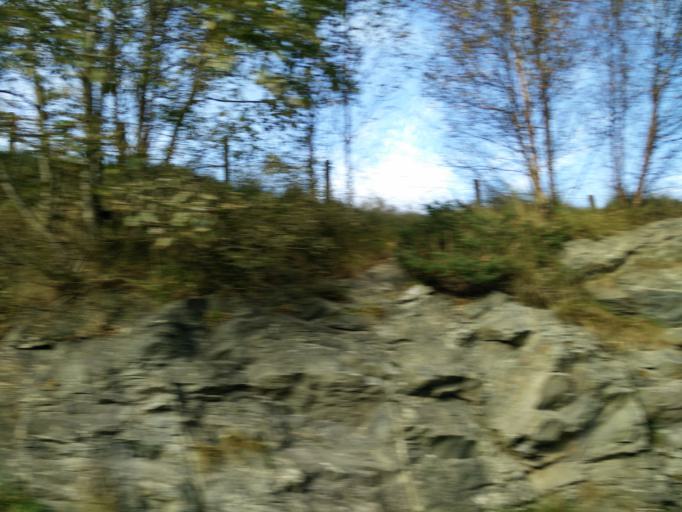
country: NO
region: Hordaland
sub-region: Sveio
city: Sveio
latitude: 59.5363
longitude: 5.3366
